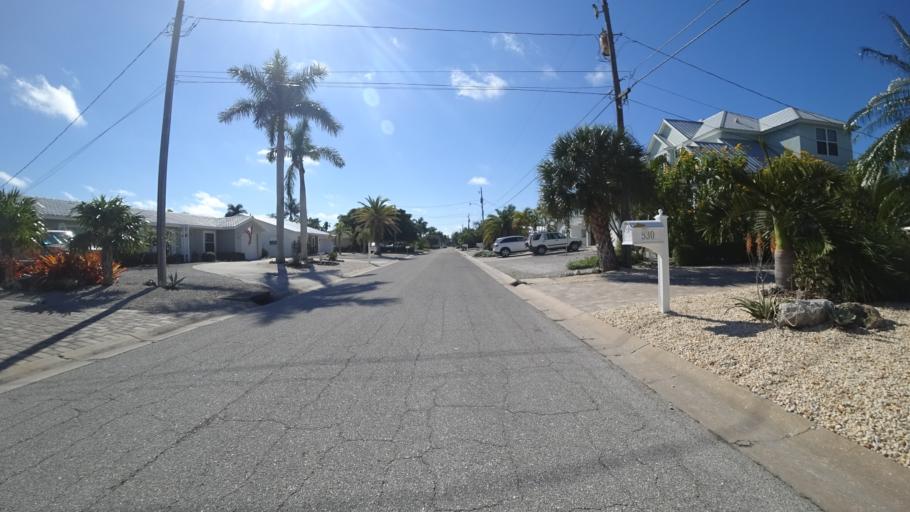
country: US
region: Florida
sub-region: Manatee County
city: Holmes Beach
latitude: 27.5169
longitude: -82.7154
